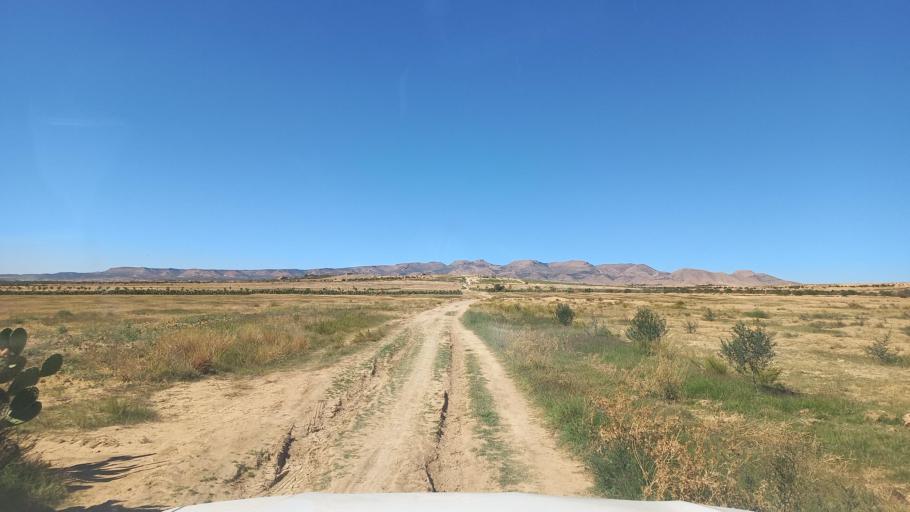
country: TN
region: Al Qasrayn
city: Sbiba
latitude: 35.3692
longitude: 9.0850
